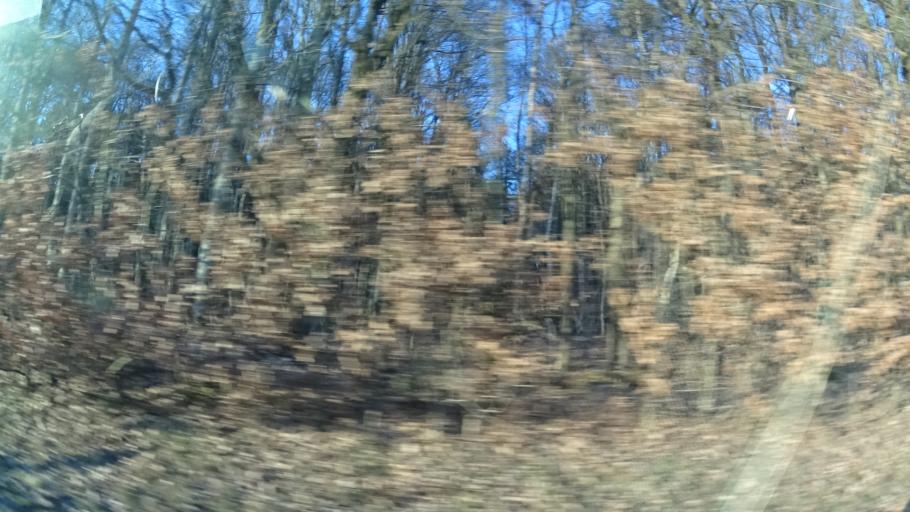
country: DE
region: Bavaria
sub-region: Regierungsbezirk Unterfranken
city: Geiselbach
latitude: 50.1282
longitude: 9.2014
